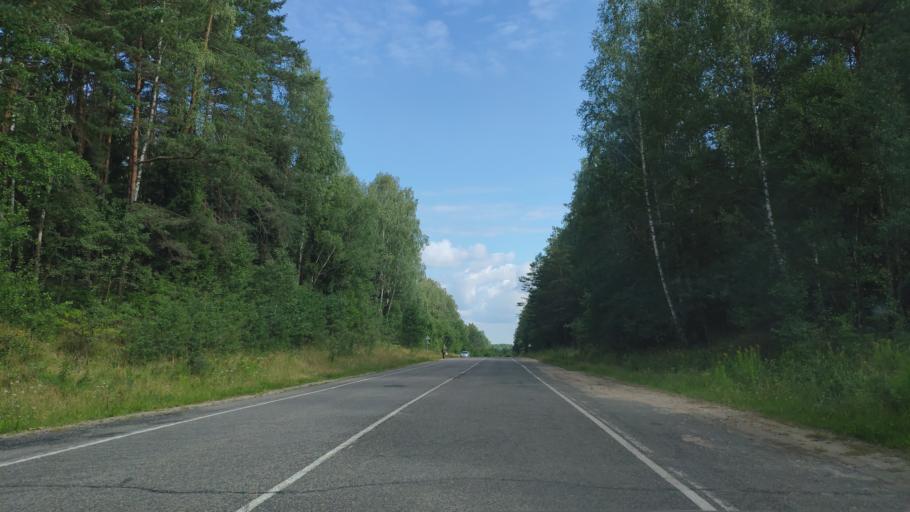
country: BY
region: Minsk
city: Khatsyezhyna
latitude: 53.9569
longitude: 27.3154
